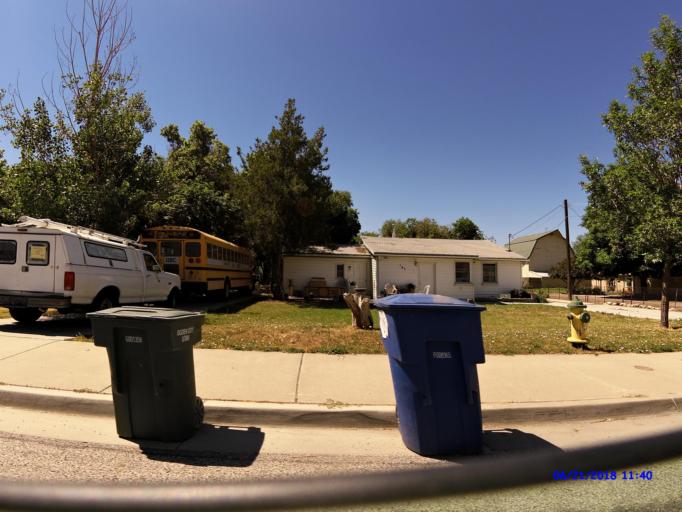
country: US
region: Utah
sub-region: Weber County
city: Harrisville
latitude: 41.2668
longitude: -111.9792
